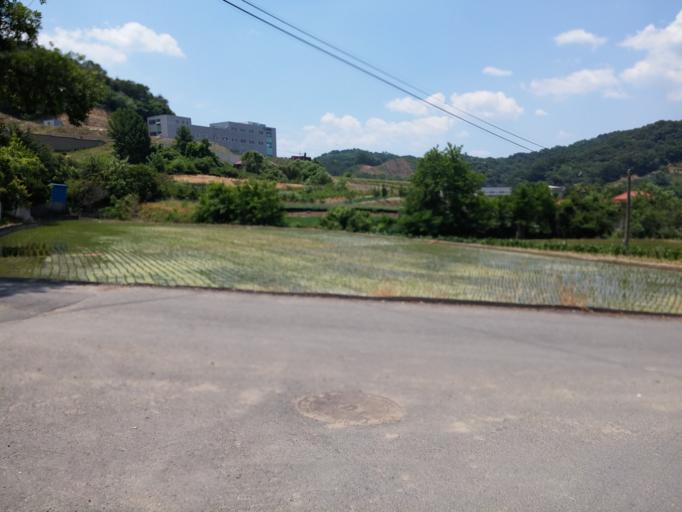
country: KR
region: Chungcheongbuk-do
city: Cheongju-si
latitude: 36.5538
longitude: 127.4360
